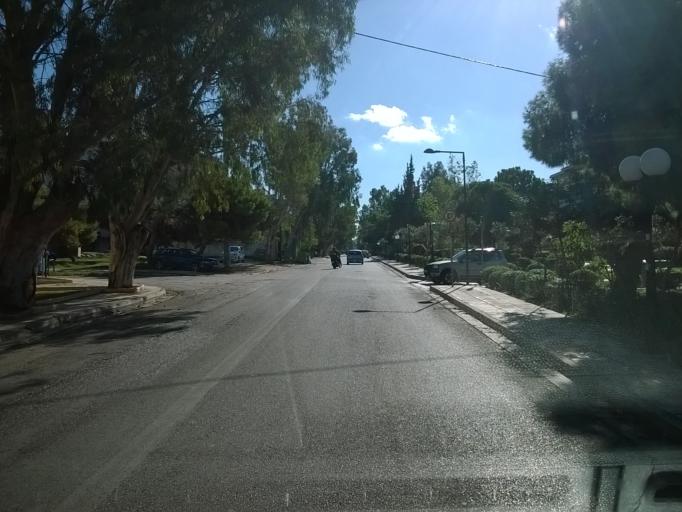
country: GR
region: Attica
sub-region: Nomarchia Athinas
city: Glyfada
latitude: 37.8466
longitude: 23.7589
